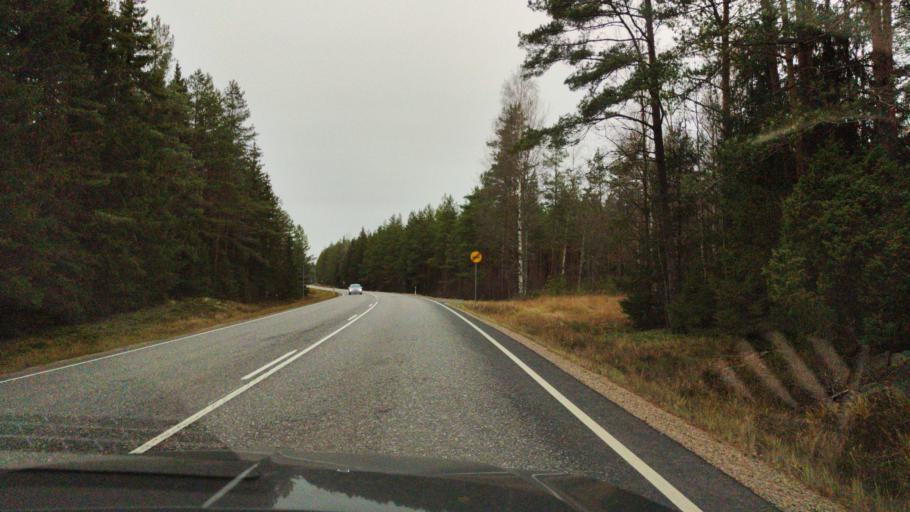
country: FI
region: Varsinais-Suomi
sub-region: Loimaa
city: Ylaene
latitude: 60.7350
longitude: 22.4336
